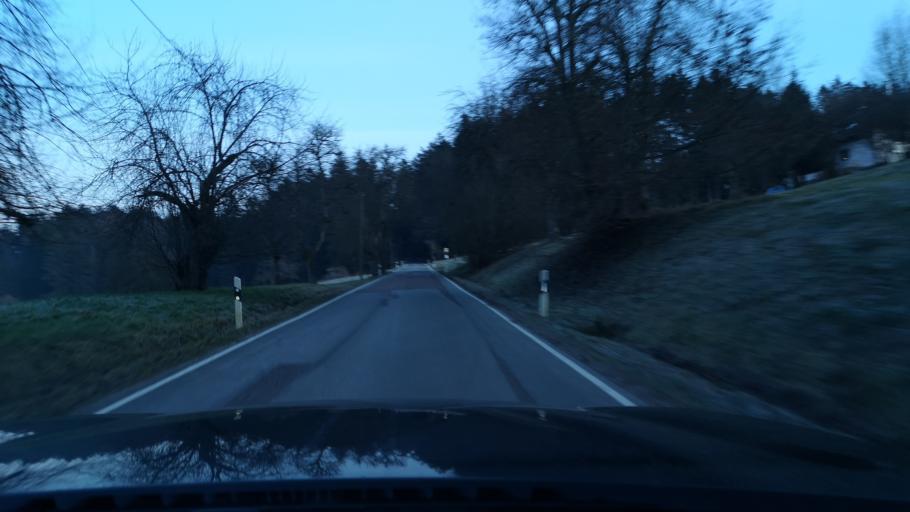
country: DE
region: Baden-Wuerttemberg
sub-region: Regierungsbezirk Stuttgart
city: Gschwend
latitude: 48.9329
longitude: 9.7036
